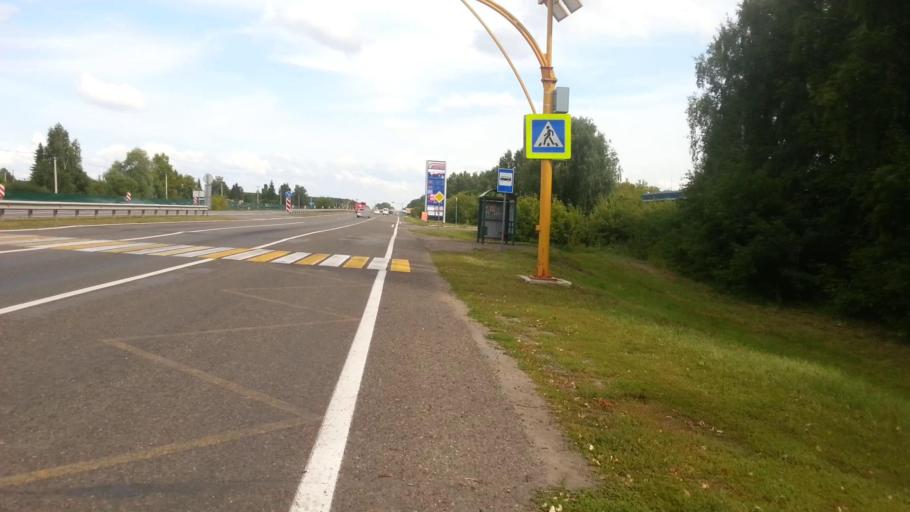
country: RU
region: Altai Krai
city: Nauchnyy Gorodok
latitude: 53.3548
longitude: 83.5346
